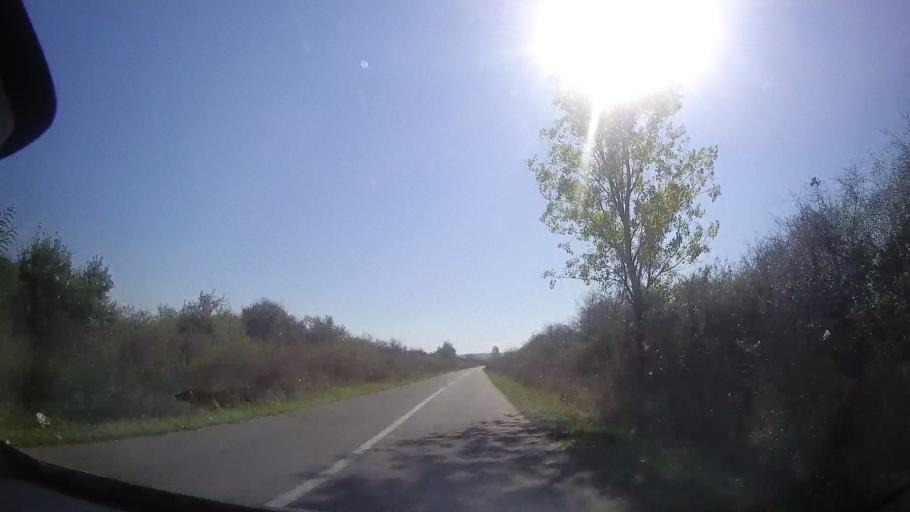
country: RO
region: Timis
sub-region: Comuna Bethausen
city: Bethausen
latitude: 45.8110
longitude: 21.9590
